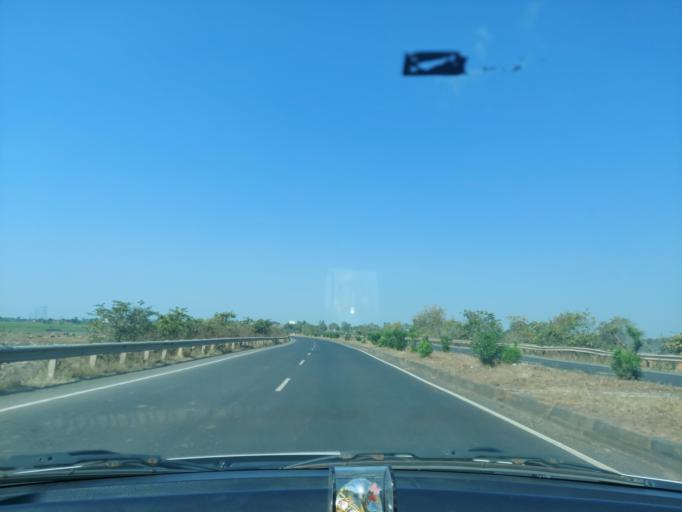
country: IN
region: Madhya Pradesh
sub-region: Indore
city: Manpur
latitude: 22.4897
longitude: 75.5671
